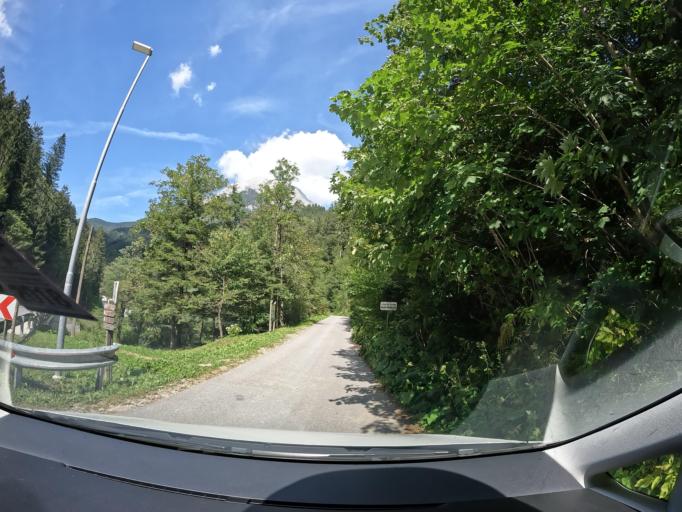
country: SI
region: Jezersko
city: Zgornje Jezersko
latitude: 46.3294
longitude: 14.4918
